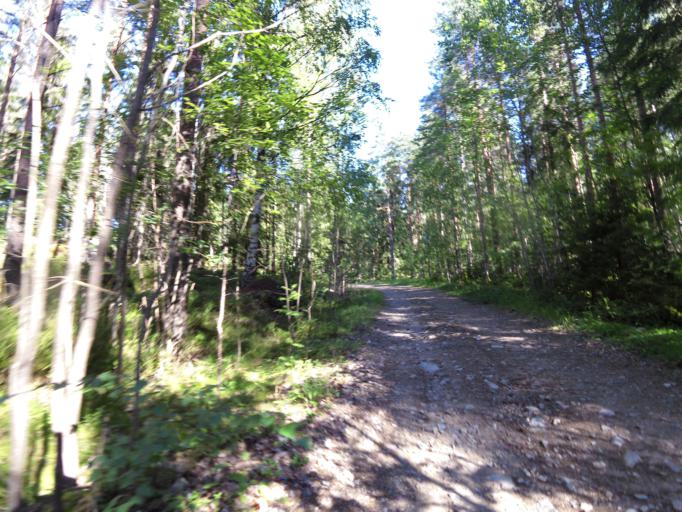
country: SE
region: Gaevleborg
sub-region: Hofors Kommun
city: Hofors
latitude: 60.5463
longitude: 16.4027
